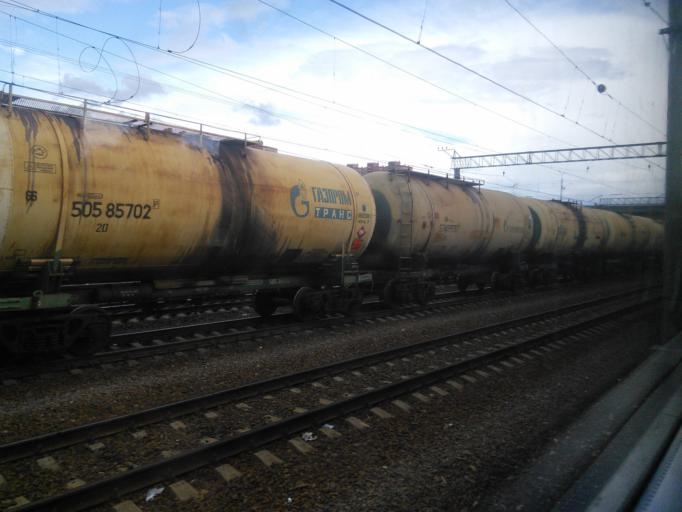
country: RU
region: Moskovskaya
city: Lyubertsy
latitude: 55.6848
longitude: 37.8918
